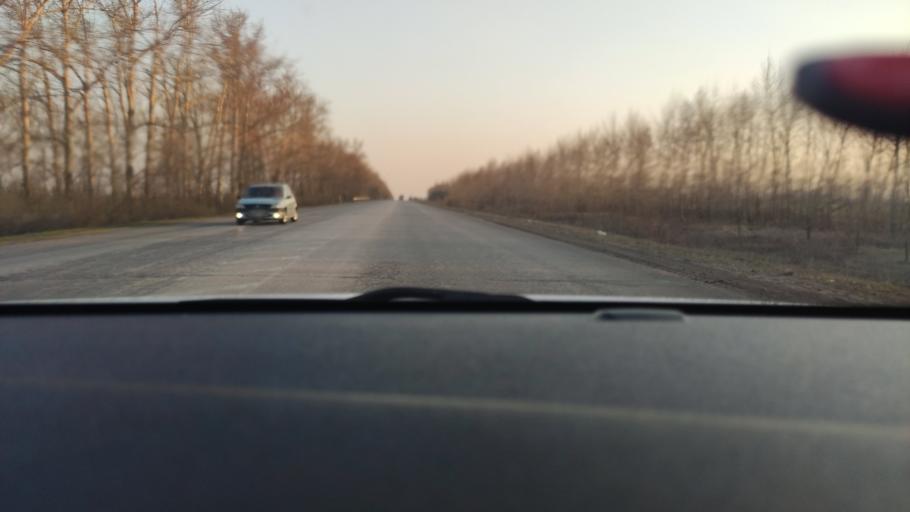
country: RU
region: Voronezj
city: Maslovka
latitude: 51.4565
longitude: 39.3042
